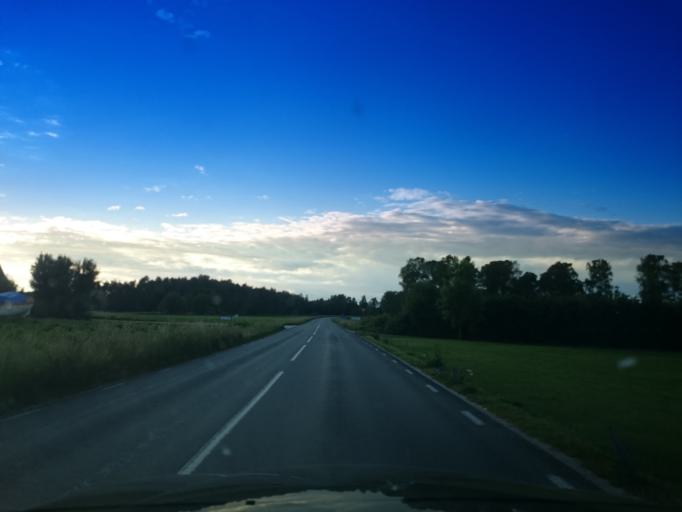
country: SE
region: Gotland
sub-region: Gotland
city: Hemse
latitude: 57.3236
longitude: 18.3836
